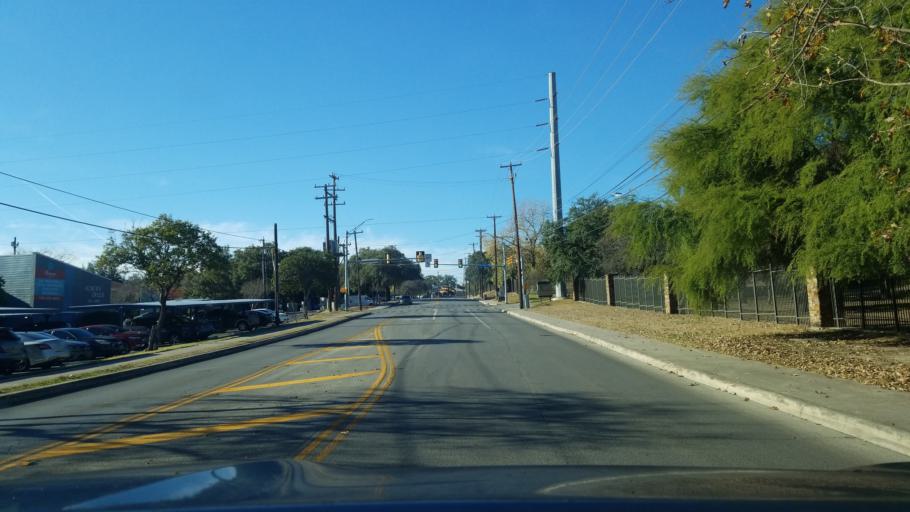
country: US
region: Texas
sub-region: Bexar County
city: Balcones Heights
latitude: 29.5285
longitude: -98.5726
